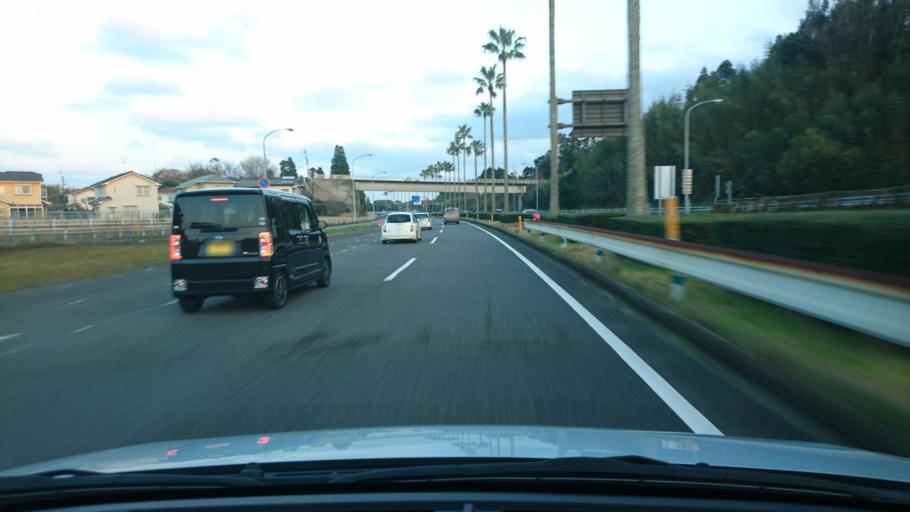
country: JP
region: Miyazaki
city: Miyazaki-shi
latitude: 31.8697
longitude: 131.4174
